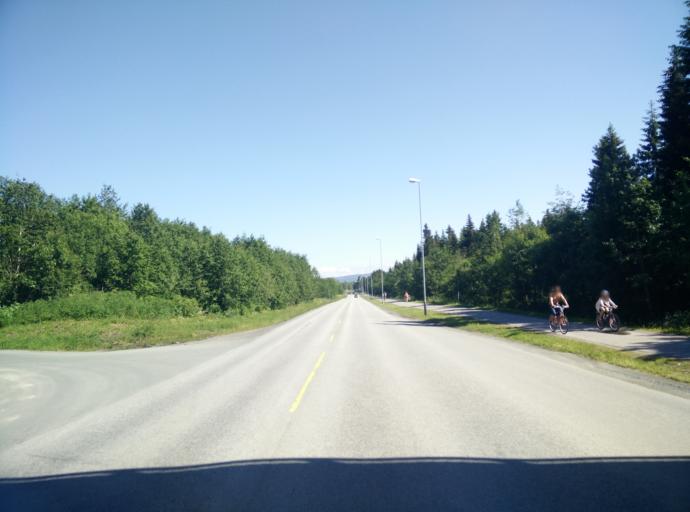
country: NO
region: Sor-Trondelag
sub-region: Trondheim
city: Trondheim
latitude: 63.3736
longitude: 10.3298
